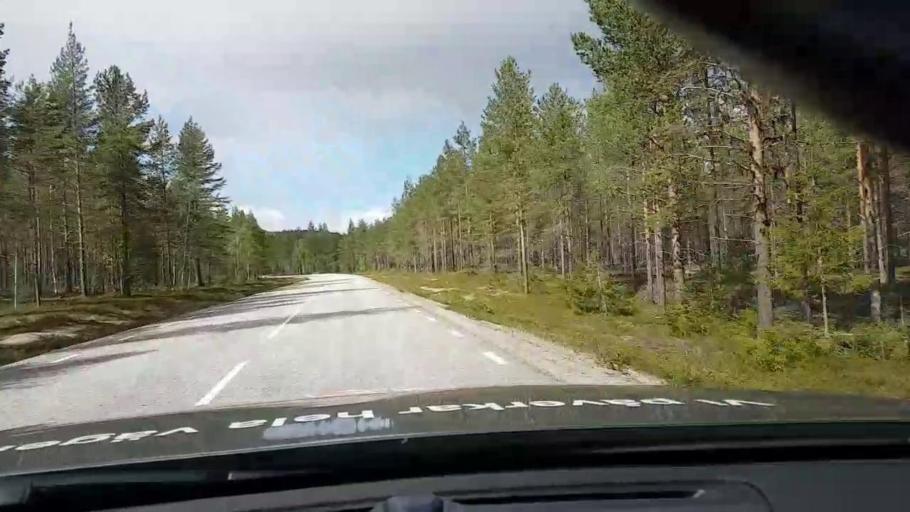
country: SE
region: Vaesternorrland
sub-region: OErnskoeldsviks Kommun
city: Bredbyn
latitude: 63.6836
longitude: 17.7789
